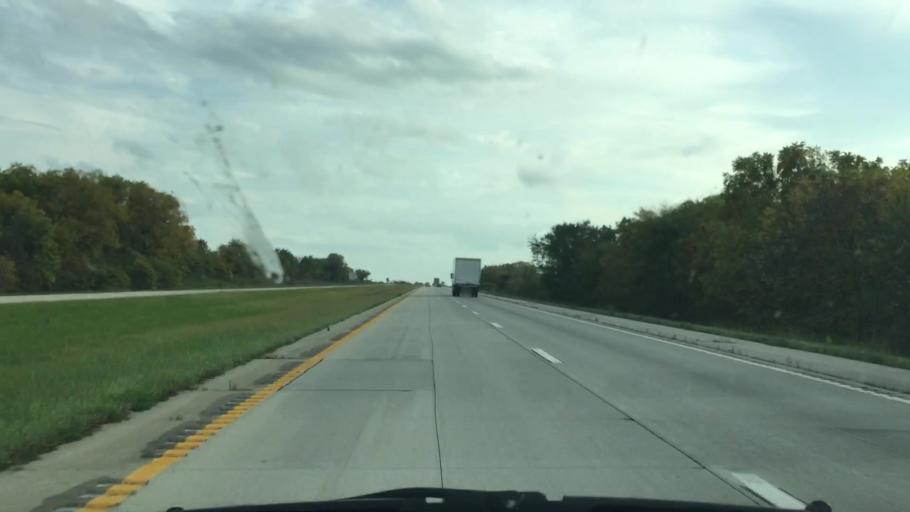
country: US
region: Missouri
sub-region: Daviess County
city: Gallatin
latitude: 39.9825
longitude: -94.0948
